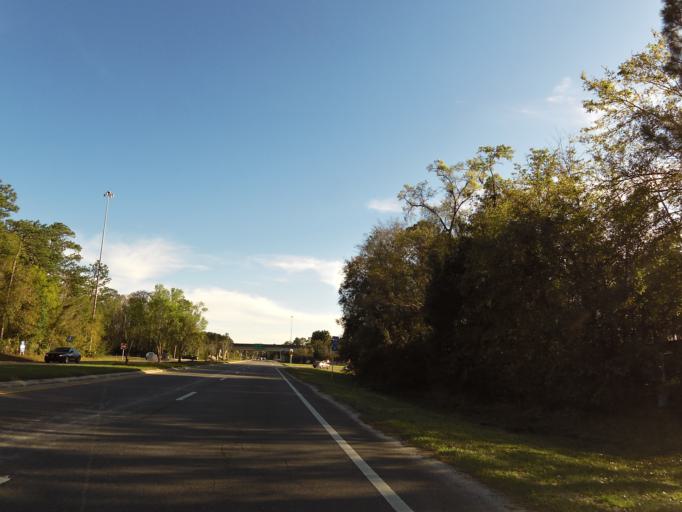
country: US
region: Florida
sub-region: Duval County
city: Jacksonville
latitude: 30.4506
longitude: -81.6132
